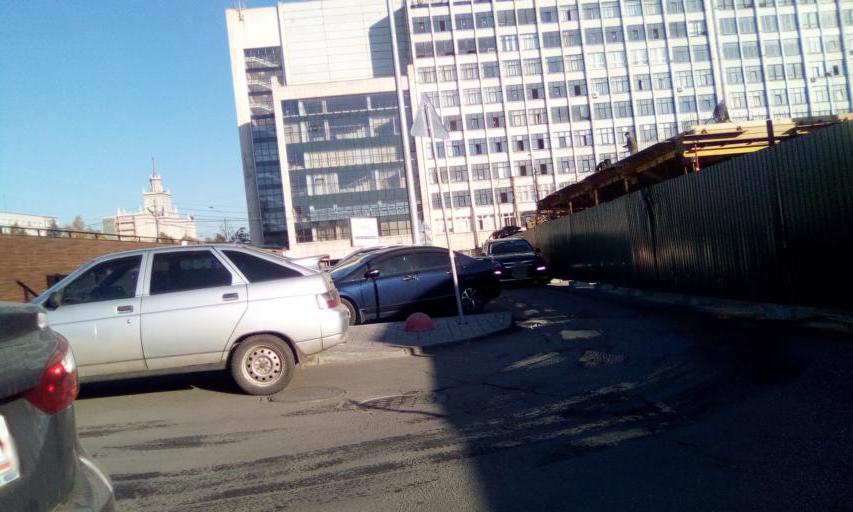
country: RU
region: Chelyabinsk
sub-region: Gorod Chelyabinsk
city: Chelyabinsk
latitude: 55.1588
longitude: 61.3633
